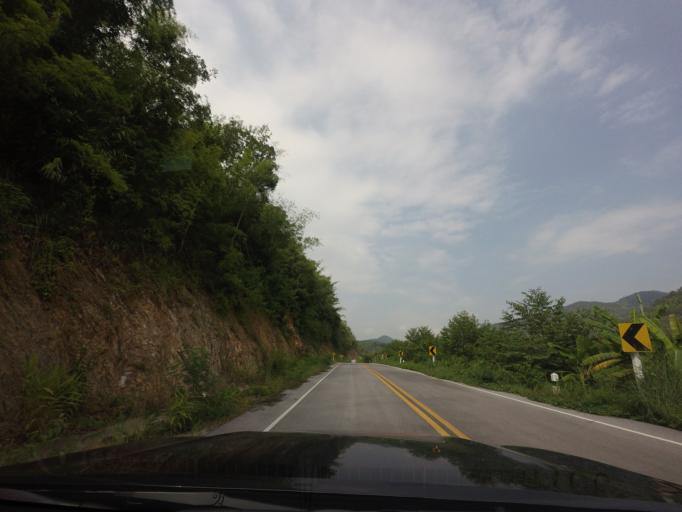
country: LA
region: Xiagnabouli
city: Muang Kenthao
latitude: 17.7740
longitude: 101.5333
